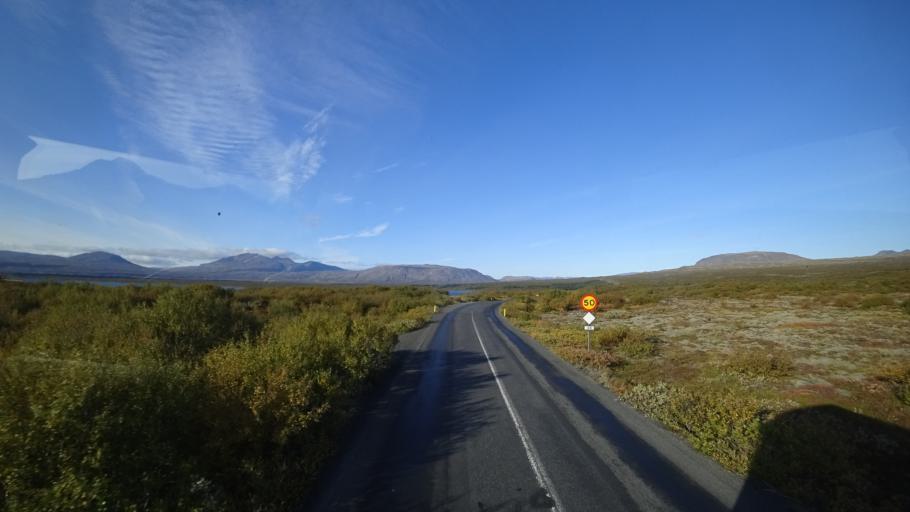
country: IS
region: South
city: Hveragerdi
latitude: 64.2285
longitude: -21.0522
